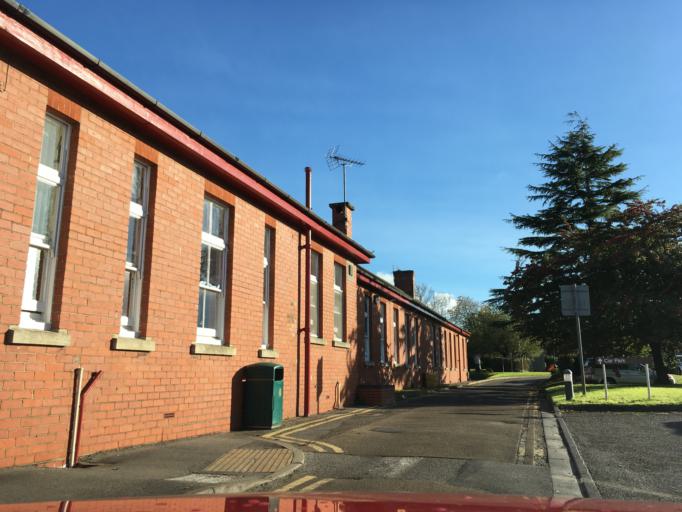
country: GB
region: England
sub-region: South Gloucestershire
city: Thornbury
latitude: 51.6118
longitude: -2.5184
